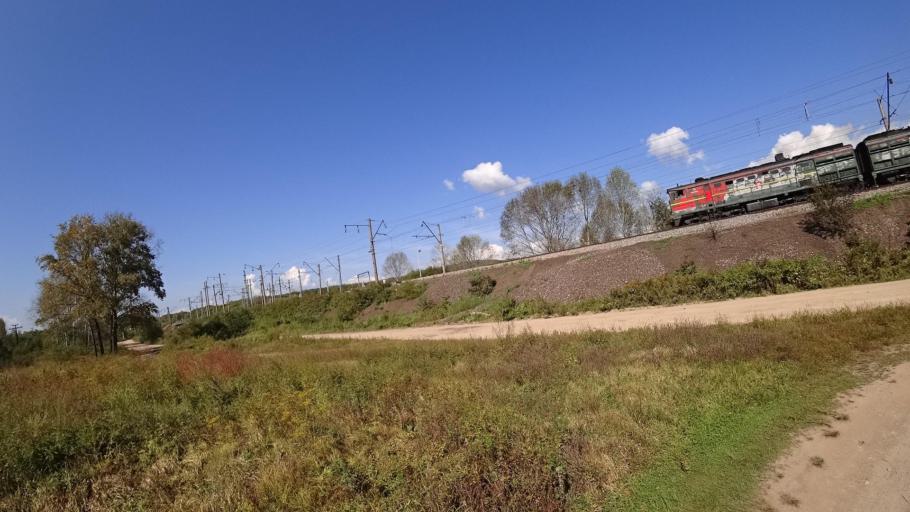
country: RU
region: Jewish Autonomous Oblast
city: Londoko
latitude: 49.0147
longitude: 132.2296
